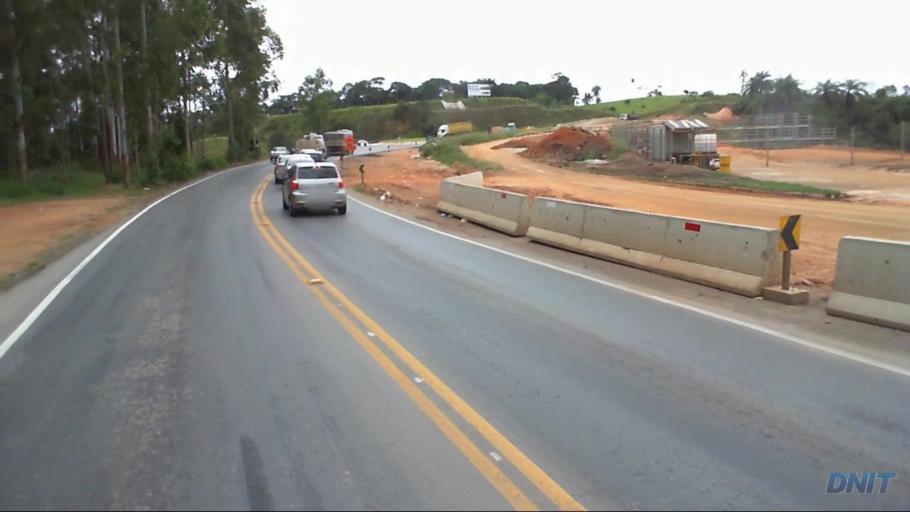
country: BR
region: Minas Gerais
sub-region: Barao De Cocais
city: Barao de Cocais
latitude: -19.7522
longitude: -43.4766
